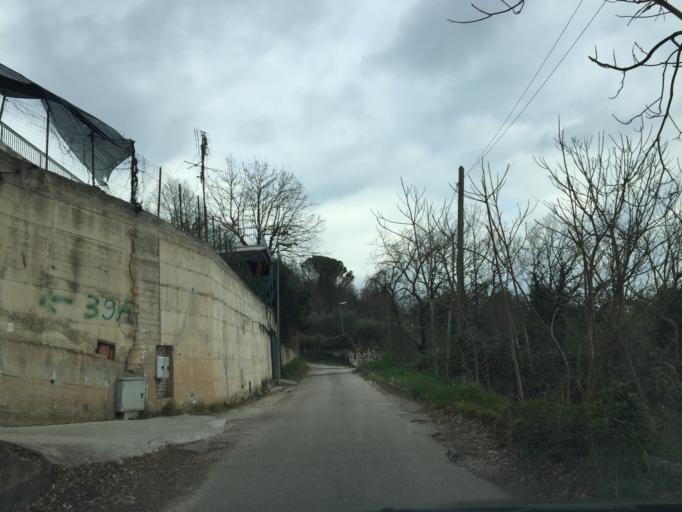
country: IT
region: Latium
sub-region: Provincia di Frosinone
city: Cassino
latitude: 41.4819
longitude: 13.8176
